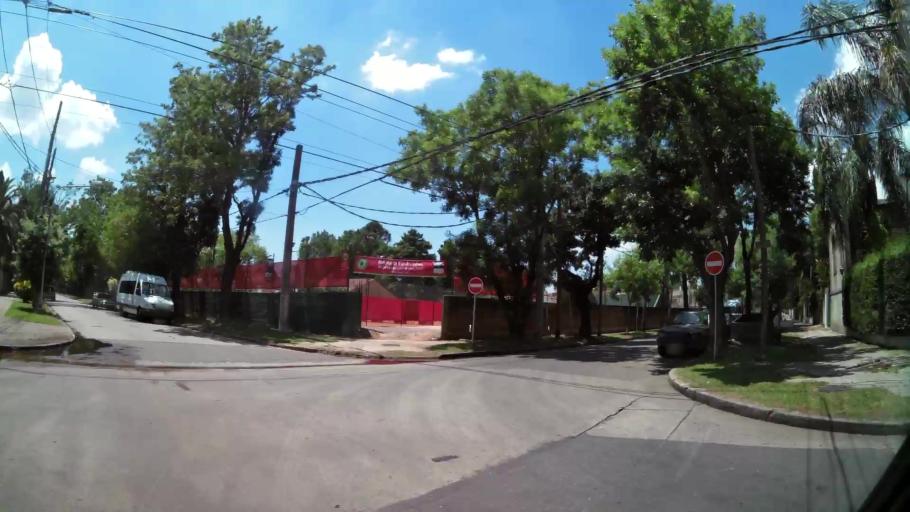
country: AR
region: Buenos Aires
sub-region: Partido de Tigre
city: Tigre
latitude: -34.4190
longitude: -58.5817
